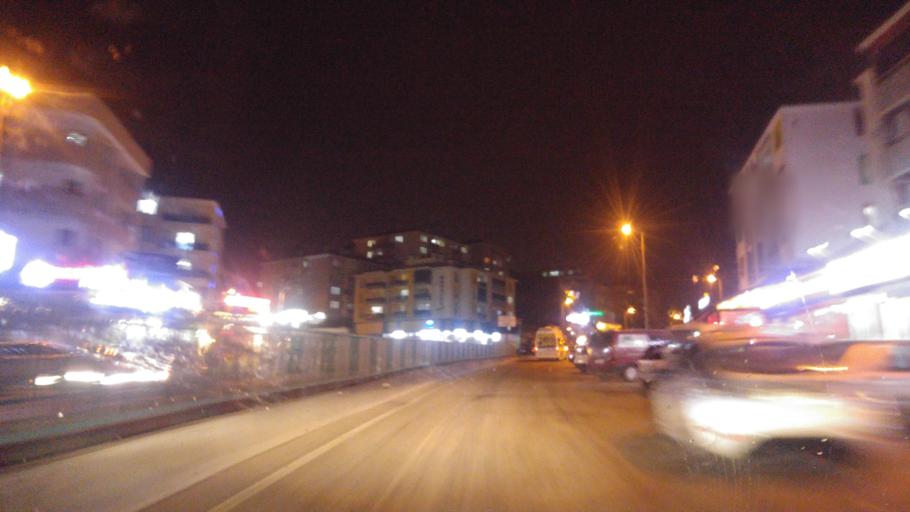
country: TR
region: Karabuk
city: Karabuk
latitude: 41.2201
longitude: 32.6604
